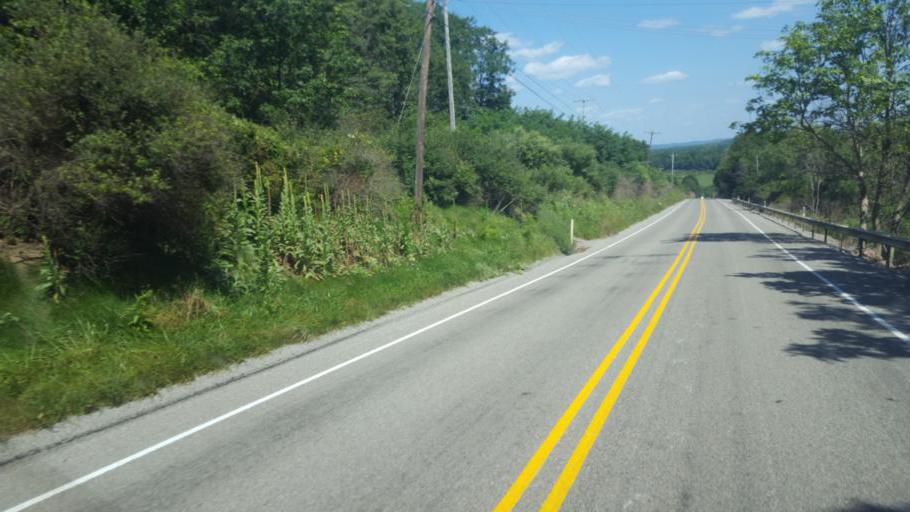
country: US
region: Pennsylvania
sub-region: Clarion County
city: Knox
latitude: 41.1093
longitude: -79.6075
